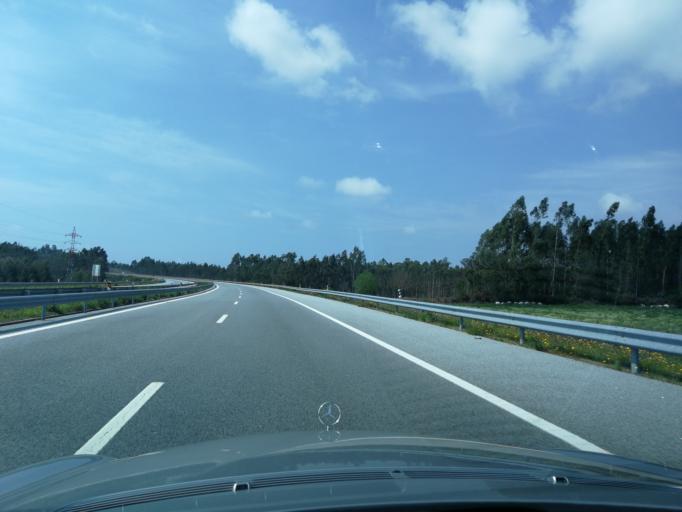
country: PT
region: Braga
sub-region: Vila Nova de Famalicao
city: Ribeirao
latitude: 41.3900
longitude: -8.5880
